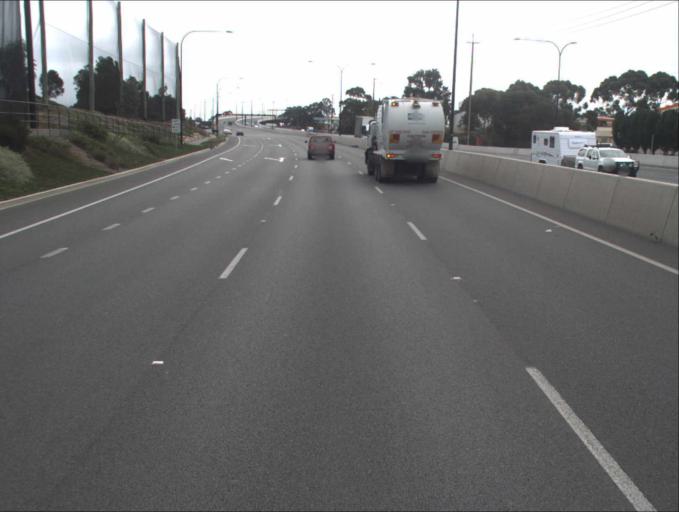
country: AU
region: South Australia
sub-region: Port Adelaide Enfield
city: Blair Athol
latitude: -34.8641
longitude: 138.5698
